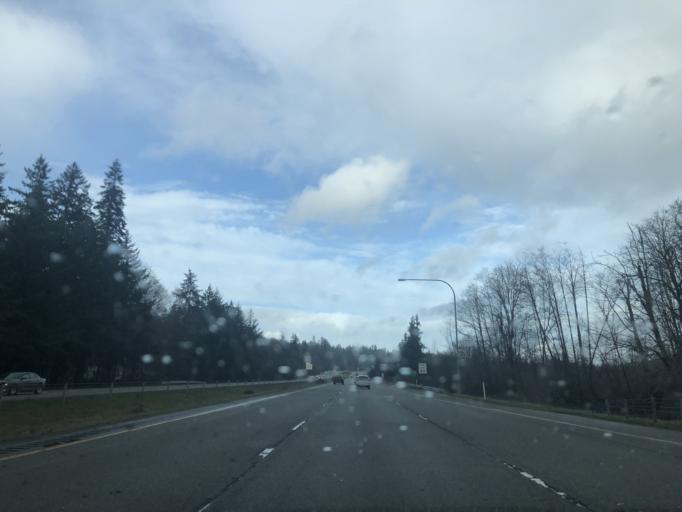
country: US
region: Washington
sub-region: Kitsap County
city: Silverdale
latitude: 47.6686
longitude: -122.6882
